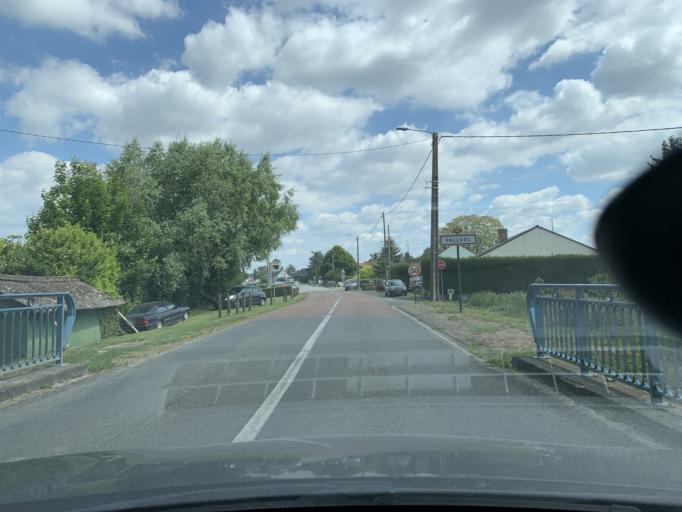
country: FR
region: Nord-Pas-de-Calais
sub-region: Departement du Nord
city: Arleux
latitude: 50.2631
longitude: 3.0928
